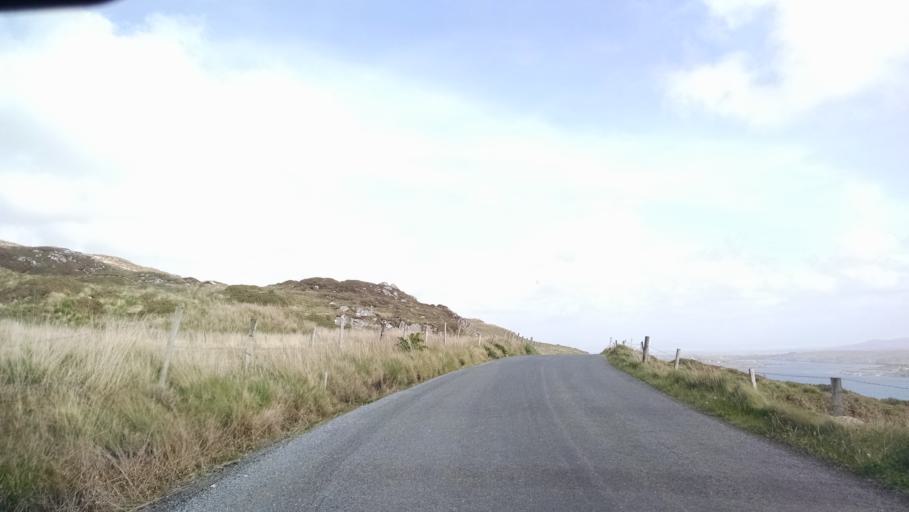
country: IE
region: Connaught
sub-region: County Galway
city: Clifden
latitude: 53.4981
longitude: -10.0867
